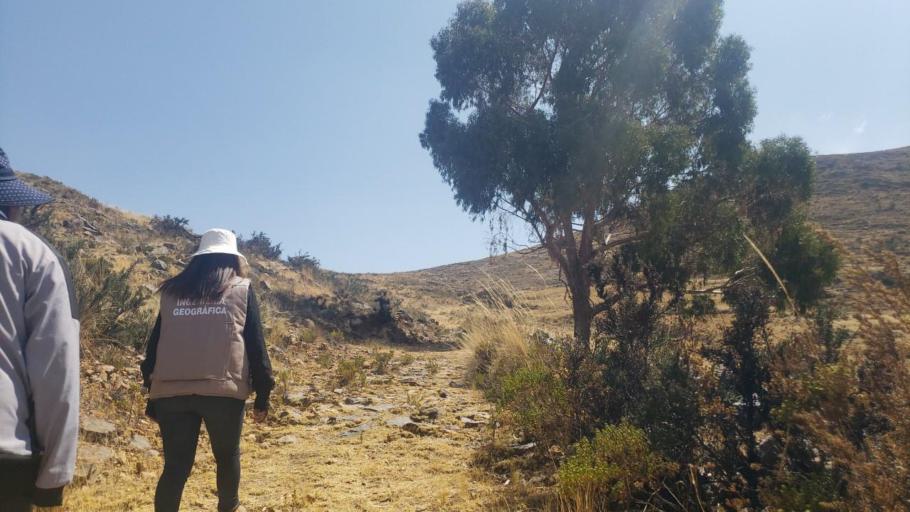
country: BO
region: La Paz
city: Batallas
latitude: -16.3495
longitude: -68.6488
